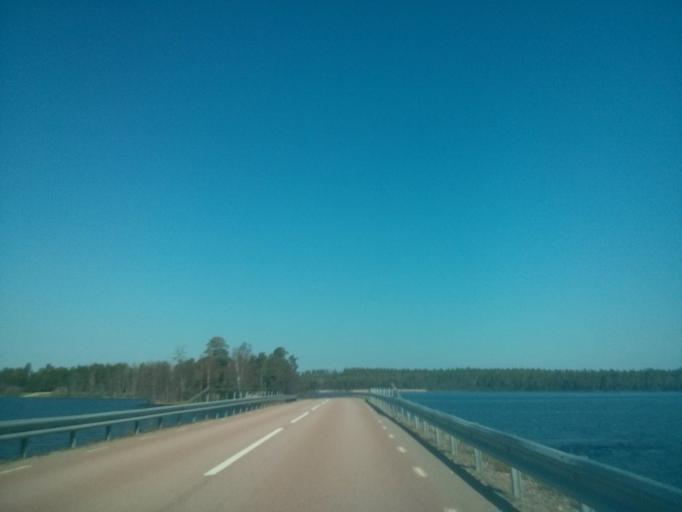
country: SE
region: Gaevleborg
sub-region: Hudiksvalls Kommun
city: Hudiksvall
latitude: 61.8818
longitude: 17.3068
